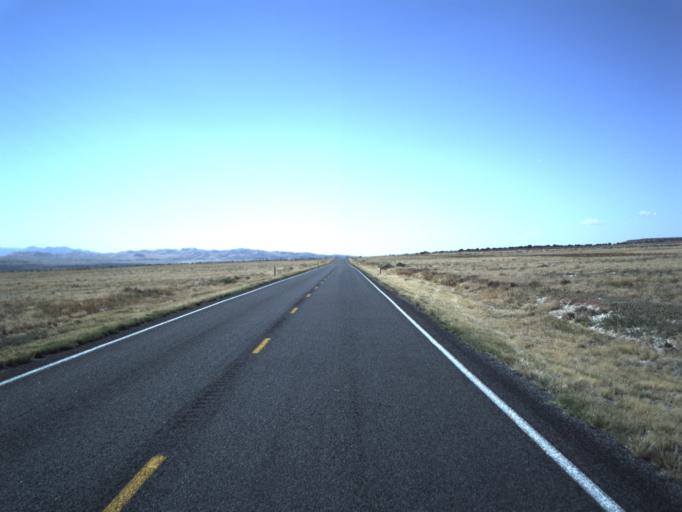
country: US
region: Utah
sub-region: Beaver County
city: Milford
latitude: 38.8576
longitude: -112.8399
